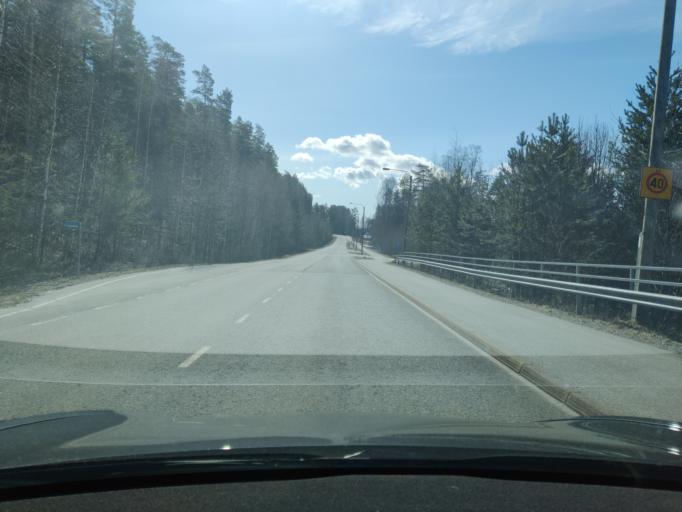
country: FI
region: Northern Savo
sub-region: Kuopio
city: Vehmersalmi
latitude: 62.7699
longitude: 28.0090
